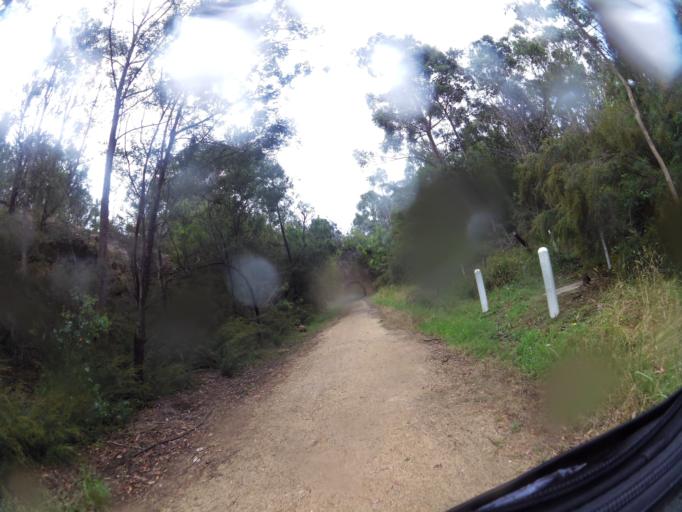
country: AU
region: Victoria
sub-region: East Gippsland
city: Lakes Entrance
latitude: -37.7661
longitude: 147.8197
